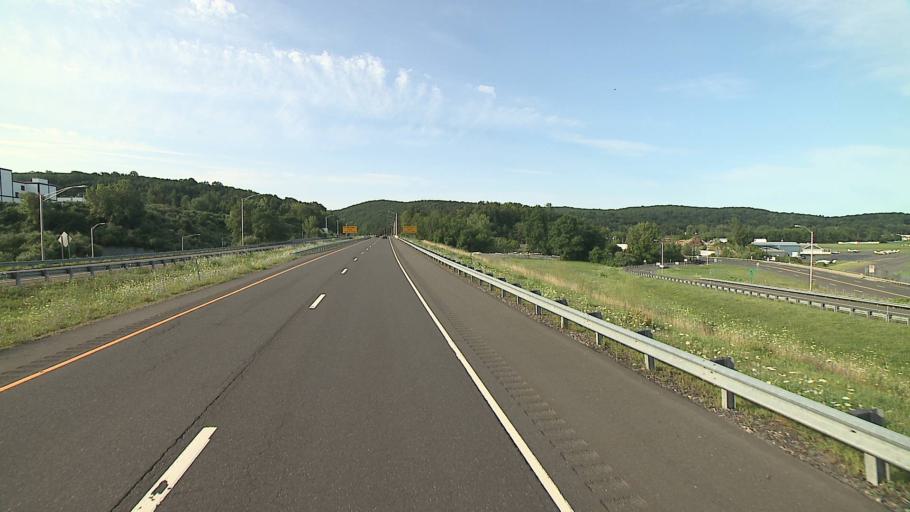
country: US
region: Connecticut
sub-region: Fairfield County
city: Danbury
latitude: 41.3731
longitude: -73.4736
